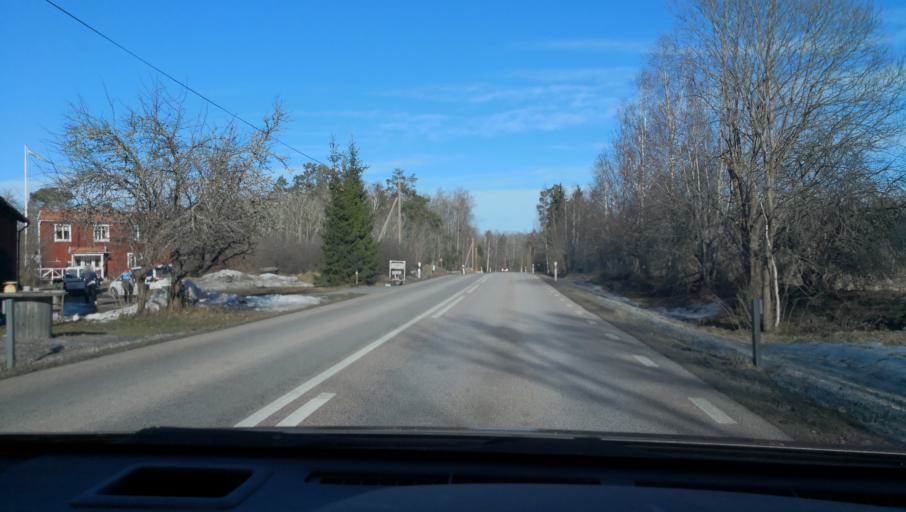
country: SE
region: Uppsala
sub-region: Osthammars Kommun
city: Osterbybruk
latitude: 60.1777
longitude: 17.8512
